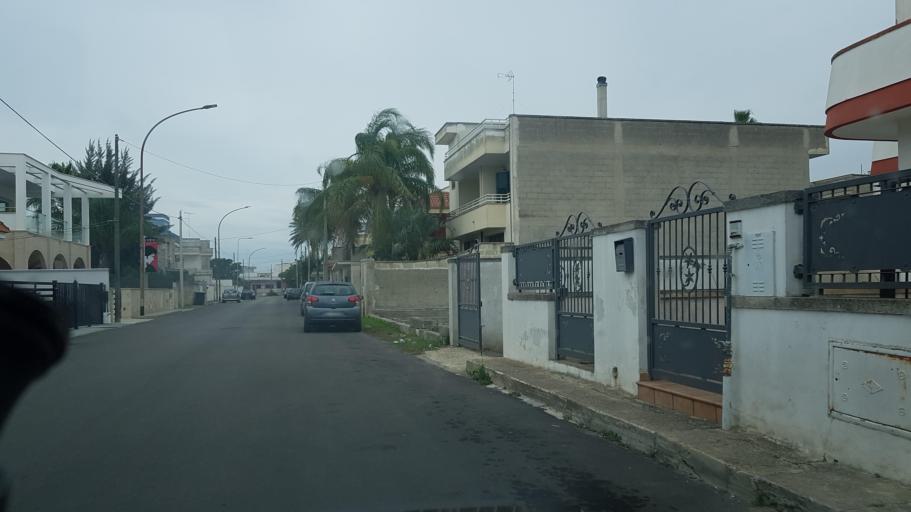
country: IT
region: Apulia
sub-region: Provincia di Lecce
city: Leverano
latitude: 40.2836
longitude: 17.9991
